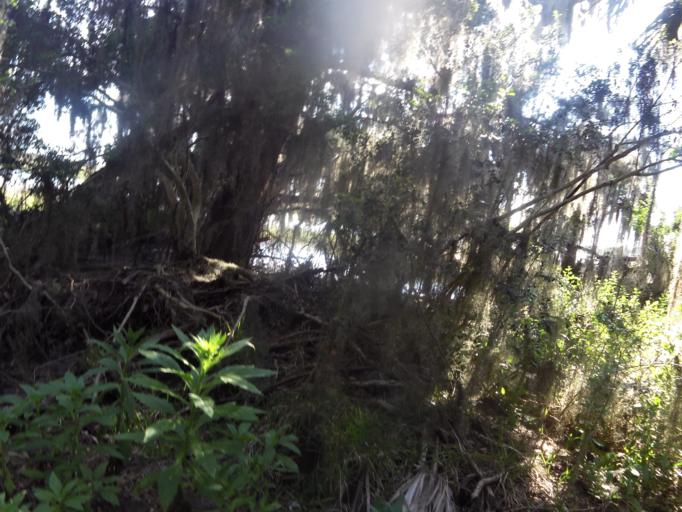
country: US
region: Florida
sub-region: Duval County
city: Atlantic Beach
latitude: 30.4373
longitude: -81.4721
